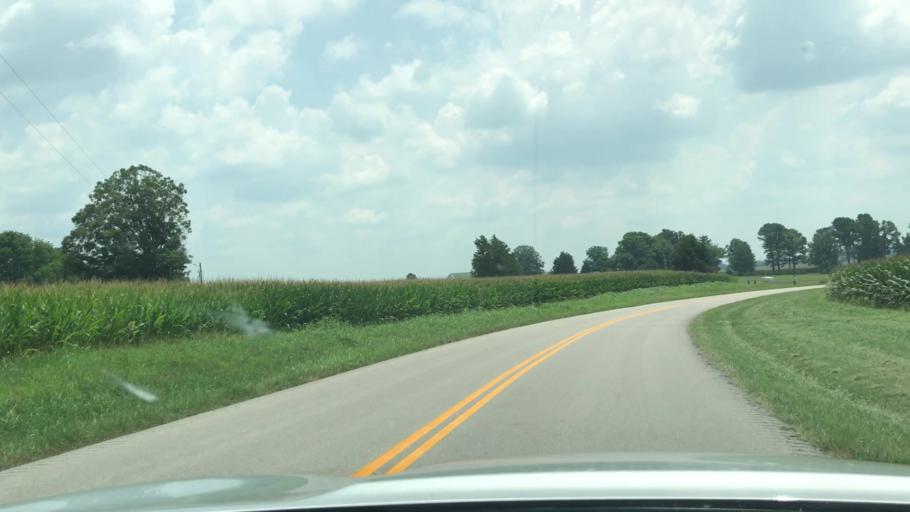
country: US
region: Kentucky
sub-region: Todd County
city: Elkton
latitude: 36.7589
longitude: -87.0971
